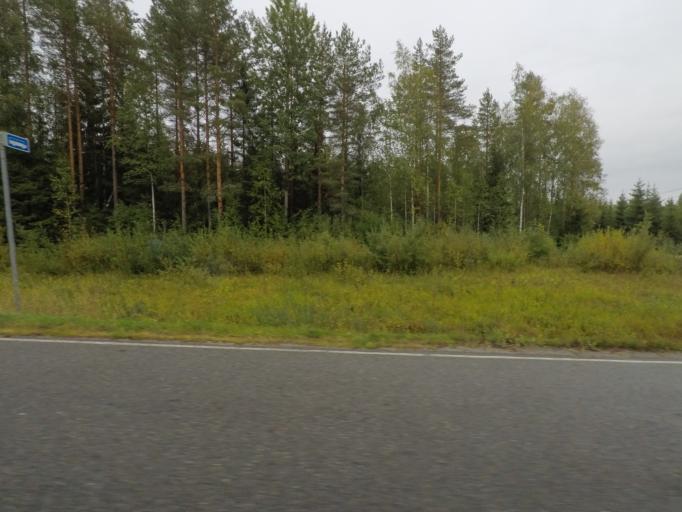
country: FI
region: Southern Savonia
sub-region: Pieksaemaeki
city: Juva
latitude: 62.0299
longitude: 27.7996
